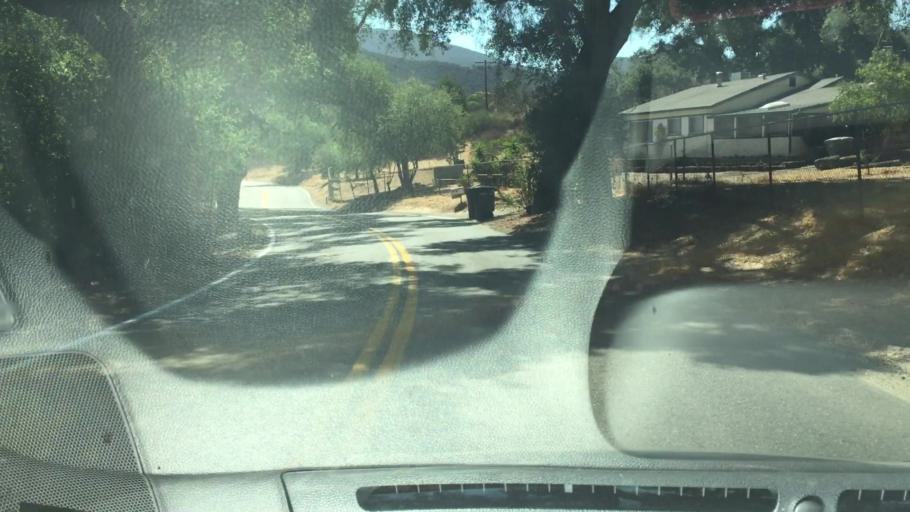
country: US
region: California
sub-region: San Diego County
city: Alpine
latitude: 32.7544
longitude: -116.7793
